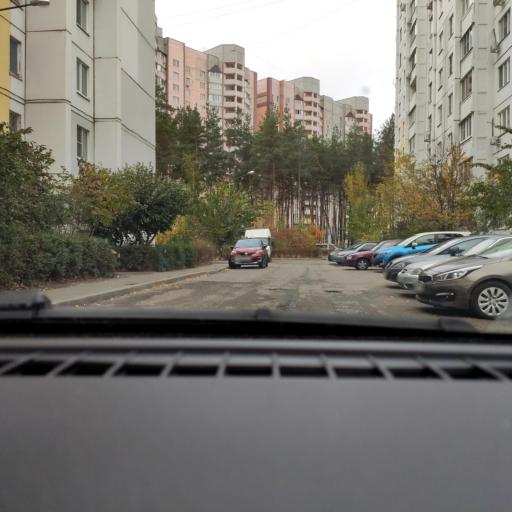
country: RU
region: Voronezj
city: Somovo
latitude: 51.6907
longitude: 39.2816
